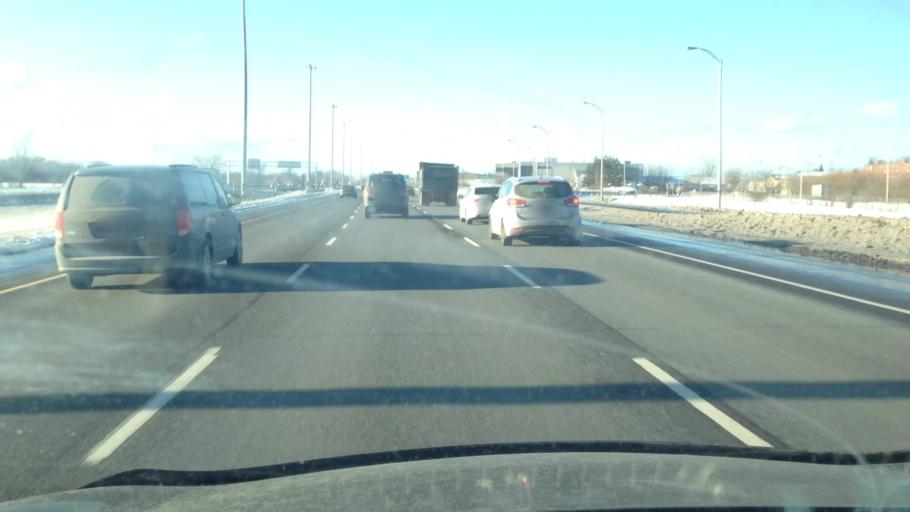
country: CA
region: Quebec
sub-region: Laurentides
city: Boisbriand
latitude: 45.6175
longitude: -73.8237
